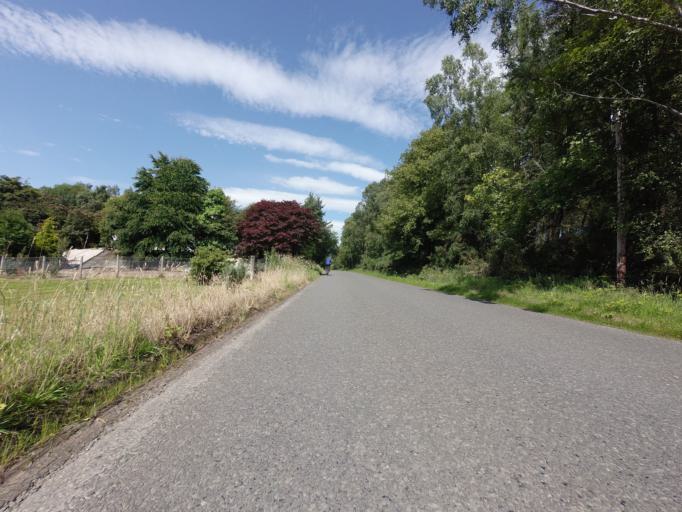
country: GB
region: Scotland
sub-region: Highland
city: Conon Bridge
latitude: 57.5368
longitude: -4.3259
